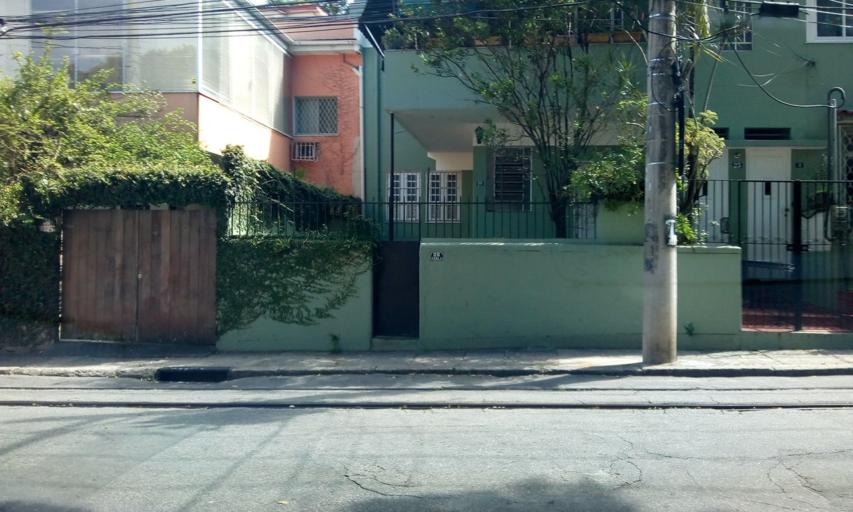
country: BR
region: Rio de Janeiro
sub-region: Rio De Janeiro
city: Rio de Janeiro
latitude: -22.9202
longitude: -43.1879
